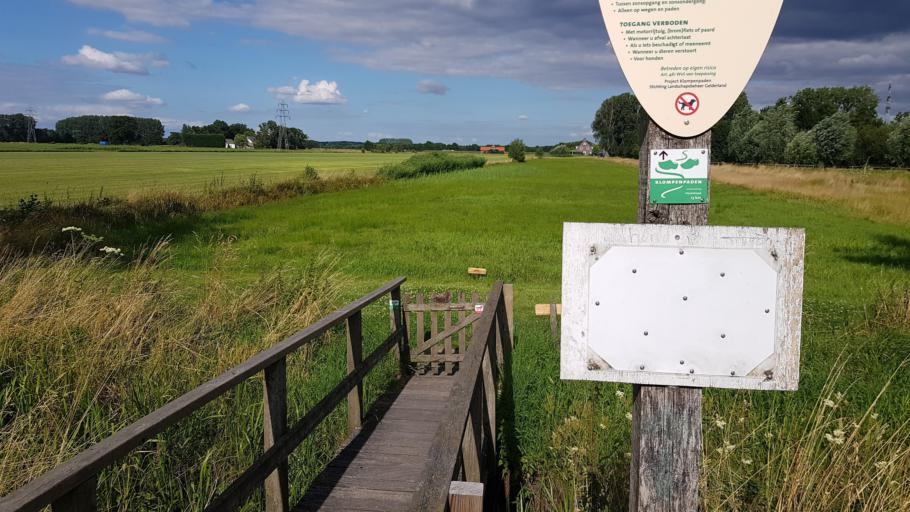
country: NL
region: Gelderland
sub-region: Gemeente Wageningen
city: Wageningen
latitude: 51.9874
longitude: 5.6325
